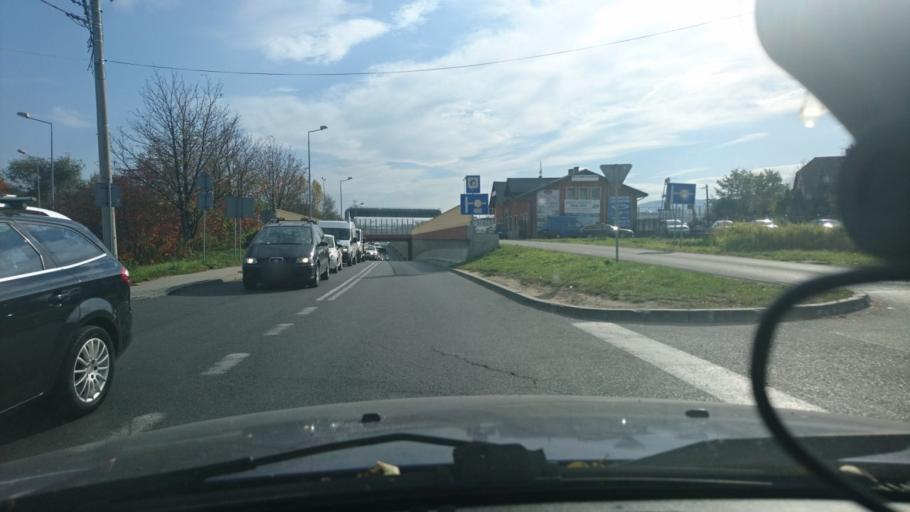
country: PL
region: Silesian Voivodeship
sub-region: Bielsko-Biala
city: Bielsko-Biala
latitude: 49.8508
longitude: 19.0355
